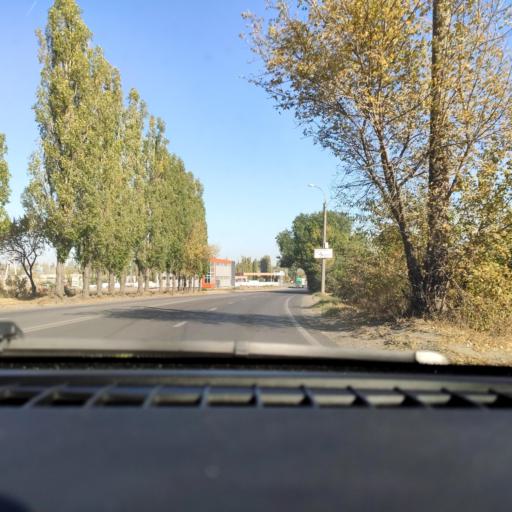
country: RU
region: Voronezj
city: Maslovka
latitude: 51.6194
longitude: 39.2591
